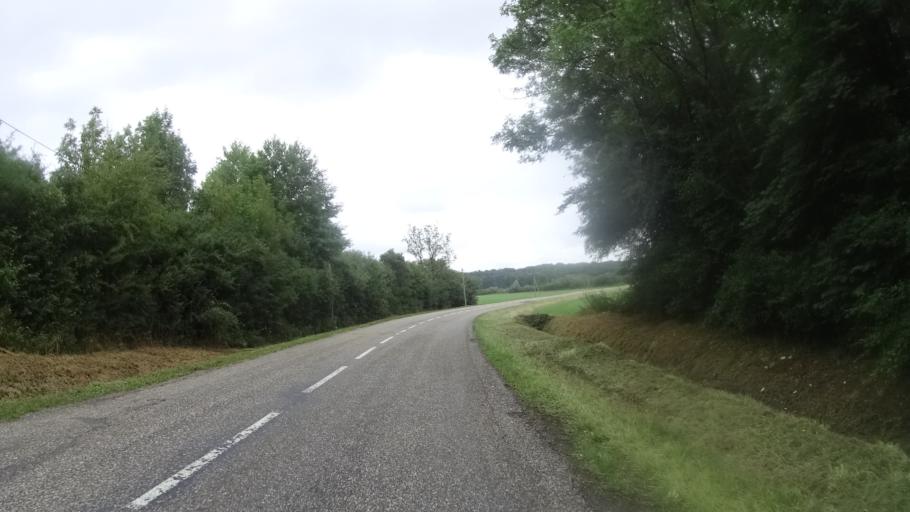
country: FR
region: Lorraine
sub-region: Departement de la Moselle
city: Dieuze
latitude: 48.6902
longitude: 6.7153
